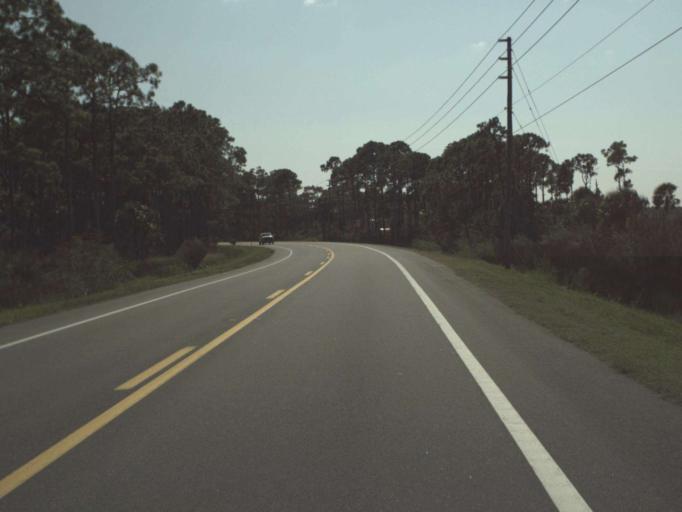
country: US
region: Florida
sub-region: Gulf County
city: Port Saint Joe
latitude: 29.7206
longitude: -85.3037
